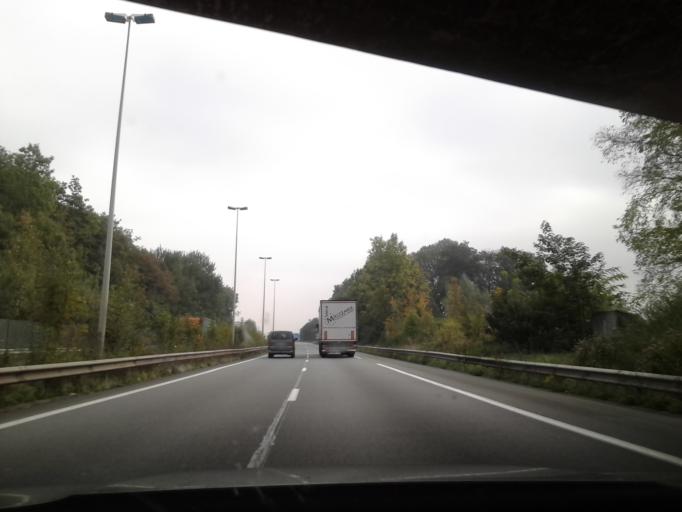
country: FR
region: Nord-Pas-de-Calais
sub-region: Departement du Nord
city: Baisieux
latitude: 50.6011
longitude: 3.2520
